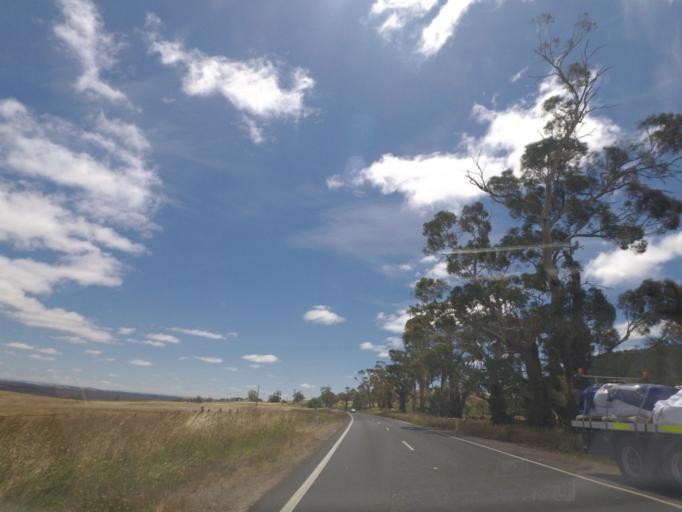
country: AU
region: Victoria
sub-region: Mount Alexander
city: Castlemaine
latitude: -37.2741
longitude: 144.1470
